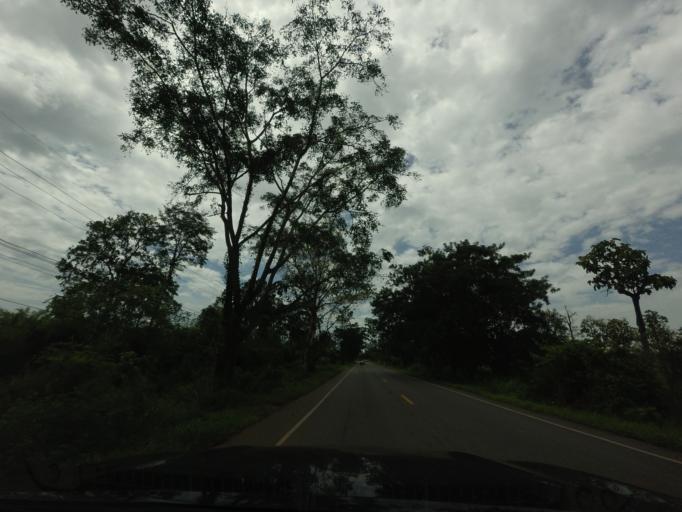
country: TH
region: Changwat Udon Thani
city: Nam Som
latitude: 17.8147
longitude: 102.2717
